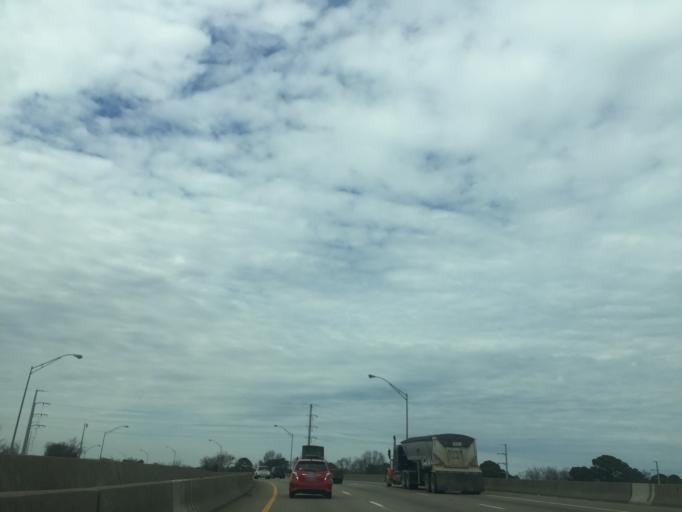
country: US
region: Virginia
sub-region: City of Hampton
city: East Hampton
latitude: 37.0282
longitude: -76.3327
